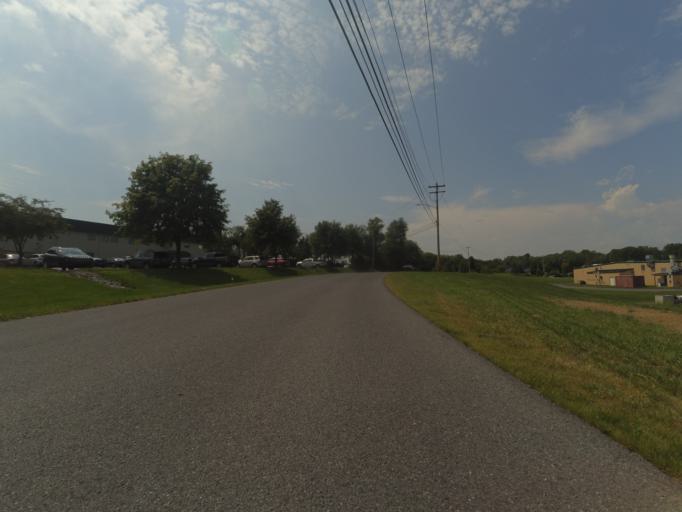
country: US
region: Pennsylvania
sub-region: Centre County
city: Bellefonte
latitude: 40.8869
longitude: -77.7691
